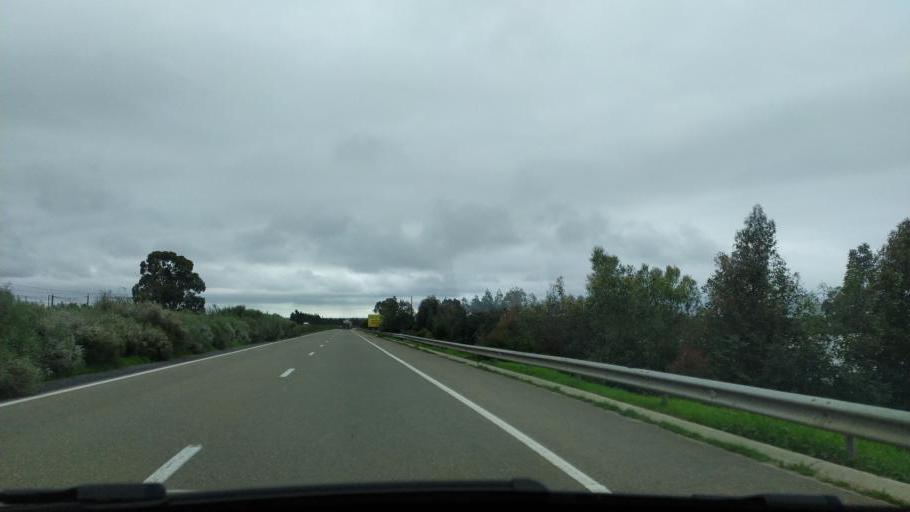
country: MA
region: Gharb-Chrarda-Beni Hssen
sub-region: Kenitra Province
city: Lalla Mimouna
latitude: 34.8893
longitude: -6.2099
